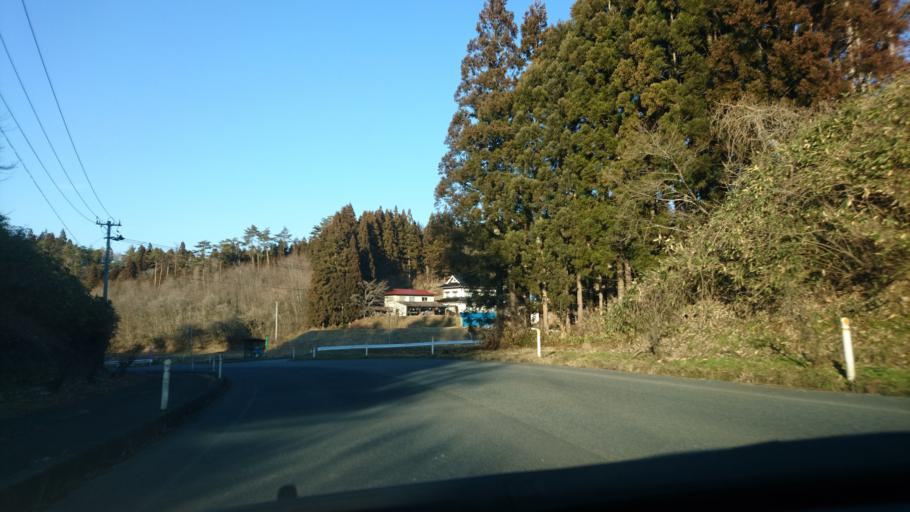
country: JP
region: Iwate
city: Ichinoseki
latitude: 38.9472
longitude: 141.3632
